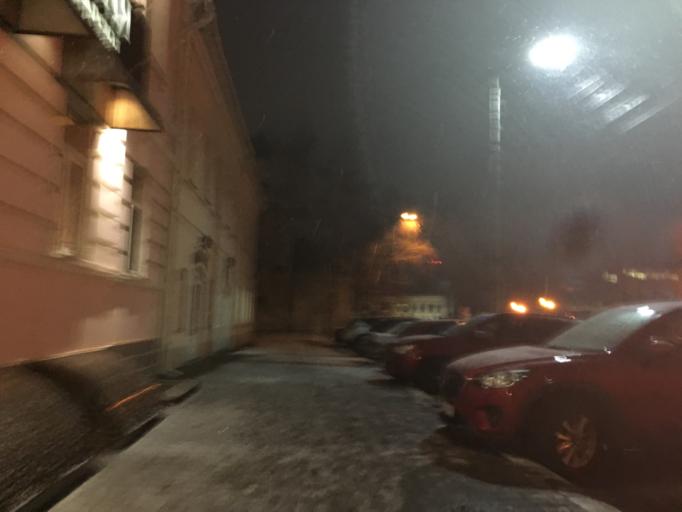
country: RU
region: Tula
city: Tula
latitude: 54.1961
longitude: 37.6163
